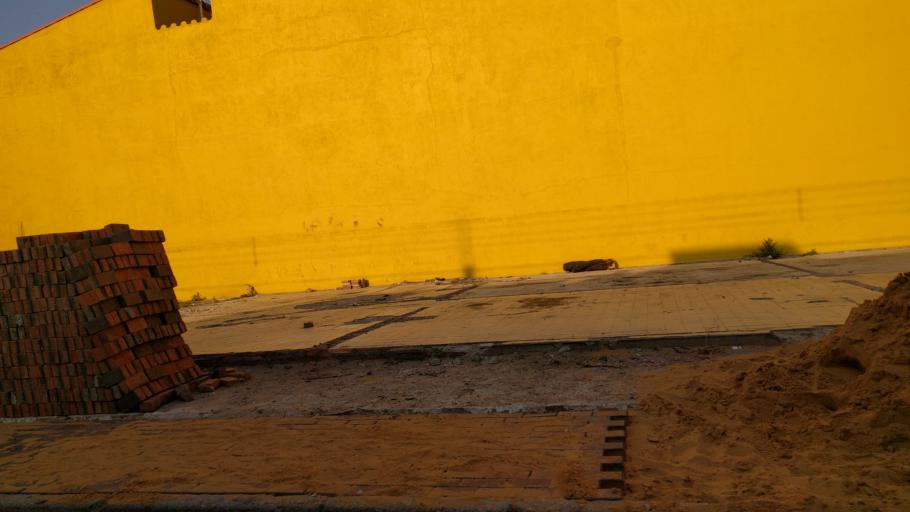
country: BO
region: Santa Cruz
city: Santa Cruz de la Sierra
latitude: -17.7992
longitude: -63.1934
